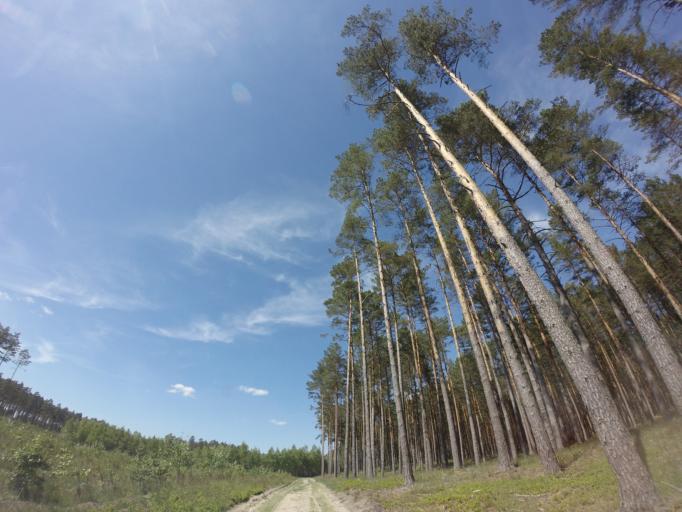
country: PL
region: West Pomeranian Voivodeship
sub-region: Powiat choszczenski
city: Drawno
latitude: 53.1390
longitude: 15.7881
